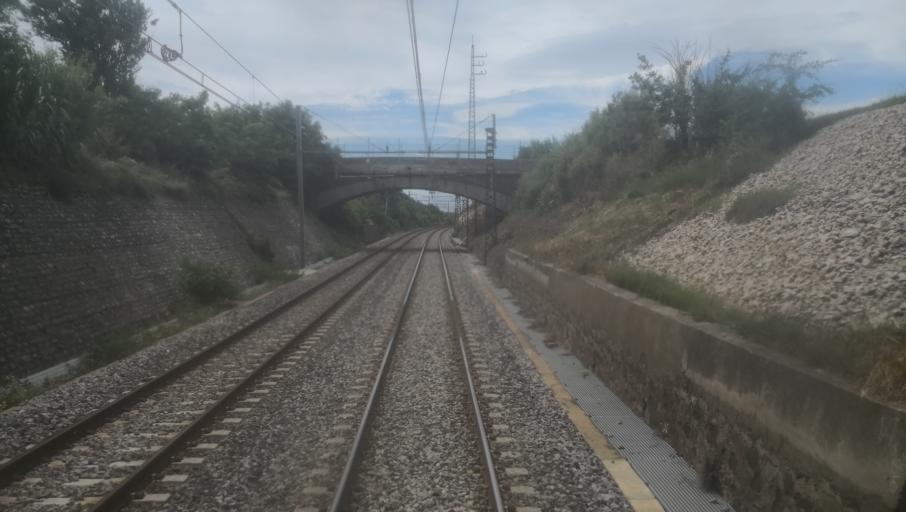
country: FR
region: Languedoc-Roussillon
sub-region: Departement de l'Herault
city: Cers
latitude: 43.3219
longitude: 3.3165
